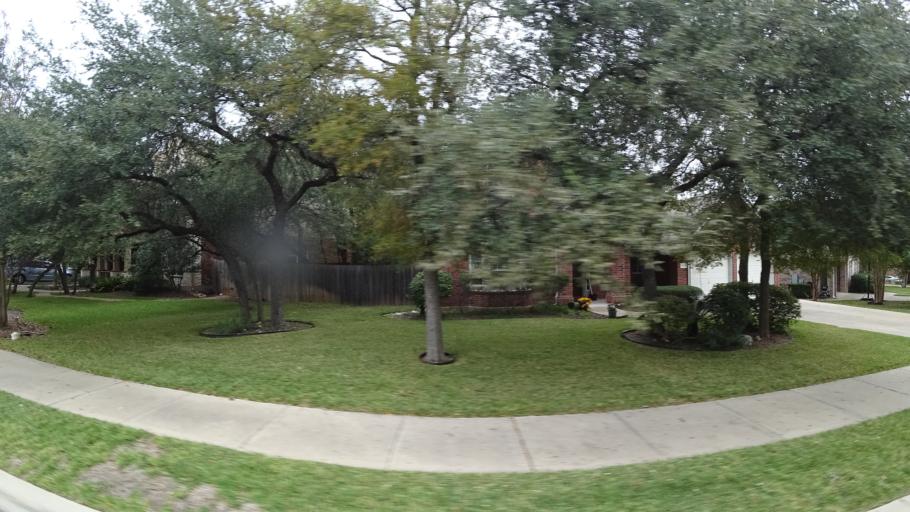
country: US
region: Texas
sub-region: Williamson County
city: Anderson Mill
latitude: 30.4307
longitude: -97.8192
